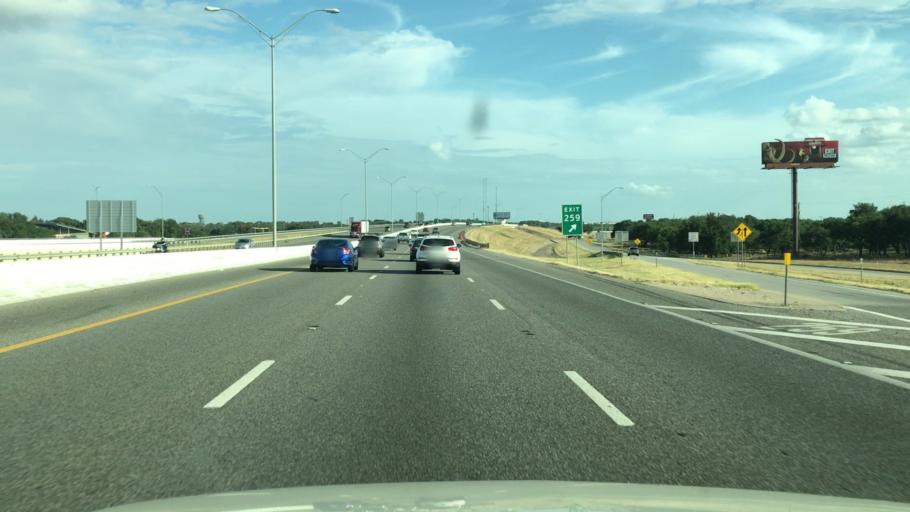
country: US
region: Texas
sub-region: Williamson County
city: Georgetown
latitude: 30.6126
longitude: -97.6874
